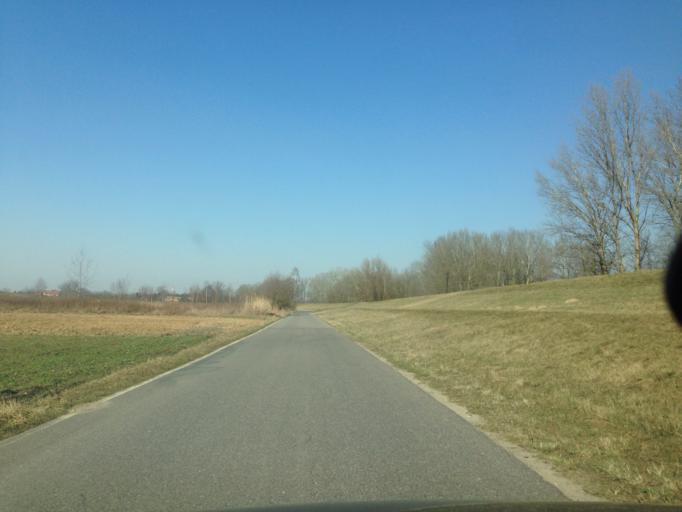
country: PL
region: Masovian Voivodeship
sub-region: Powiat piaseczynski
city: Konstancin-Jeziorna
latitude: 52.1344
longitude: 21.1655
